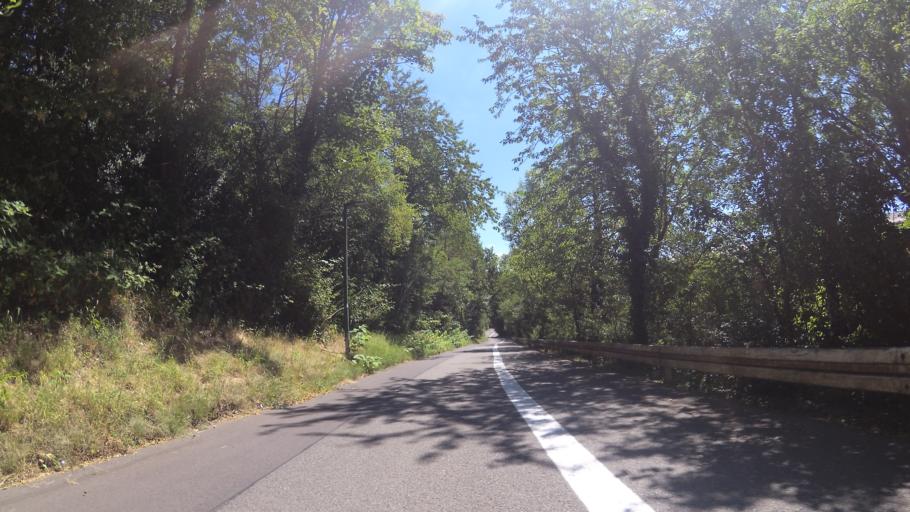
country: DE
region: Saarland
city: Neunkirchen
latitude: 49.3543
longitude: 7.1860
